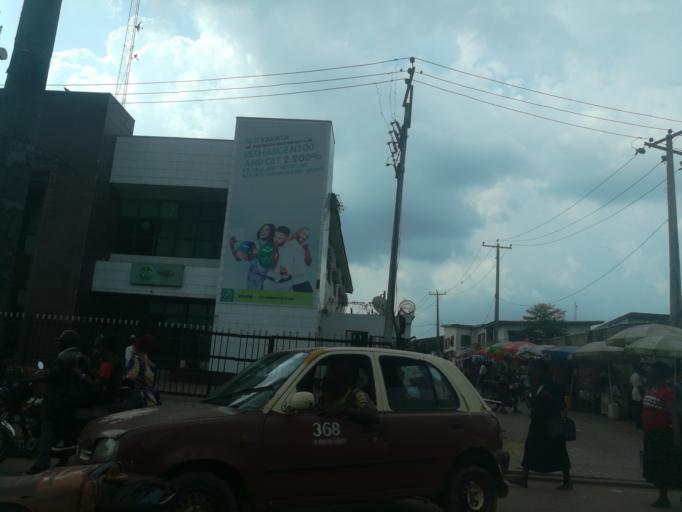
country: NG
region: Oyo
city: Ibadan
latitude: 7.3471
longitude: 3.8784
